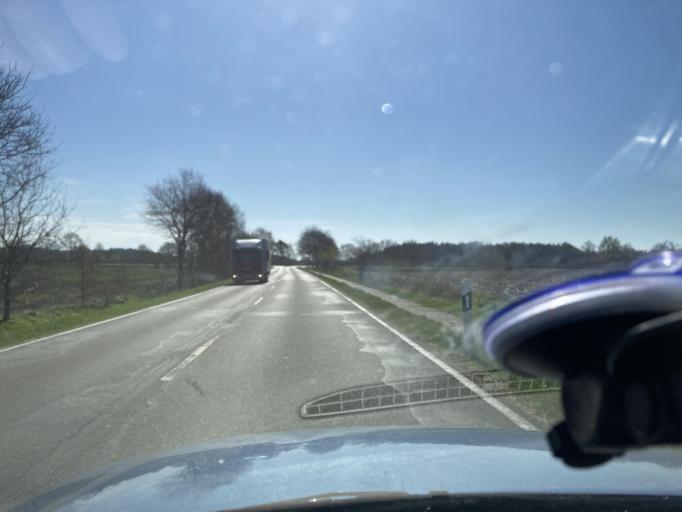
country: DE
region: Schleswig-Holstein
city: Sarzbuttel
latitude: 54.1079
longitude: 9.1923
